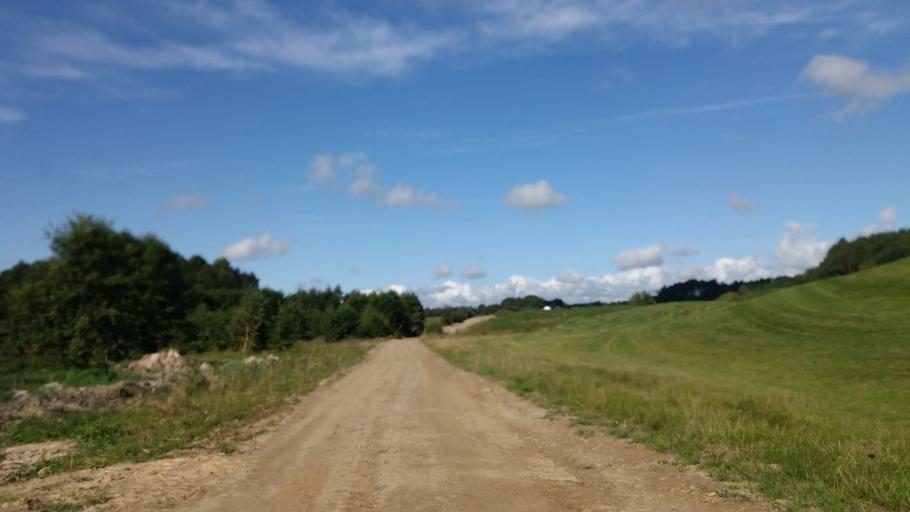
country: PL
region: West Pomeranian Voivodeship
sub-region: Powiat choszczenski
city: Krzecin
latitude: 53.1307
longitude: 15.4953
